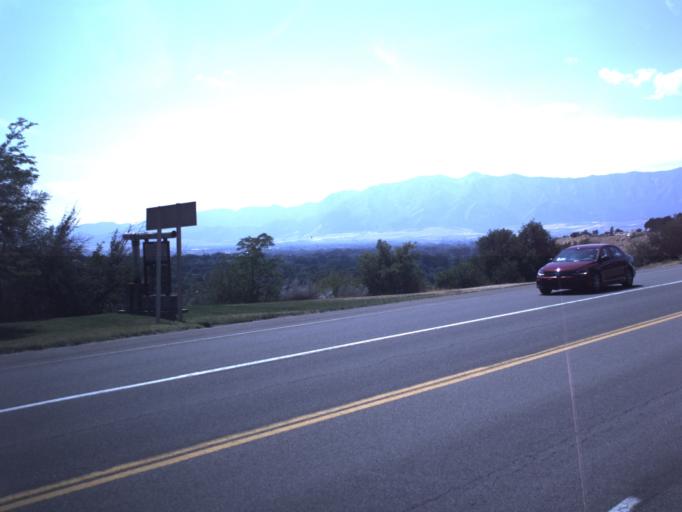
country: US
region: Utah
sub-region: Cache County
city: North Logan
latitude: 41.7438
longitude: -111.7976
